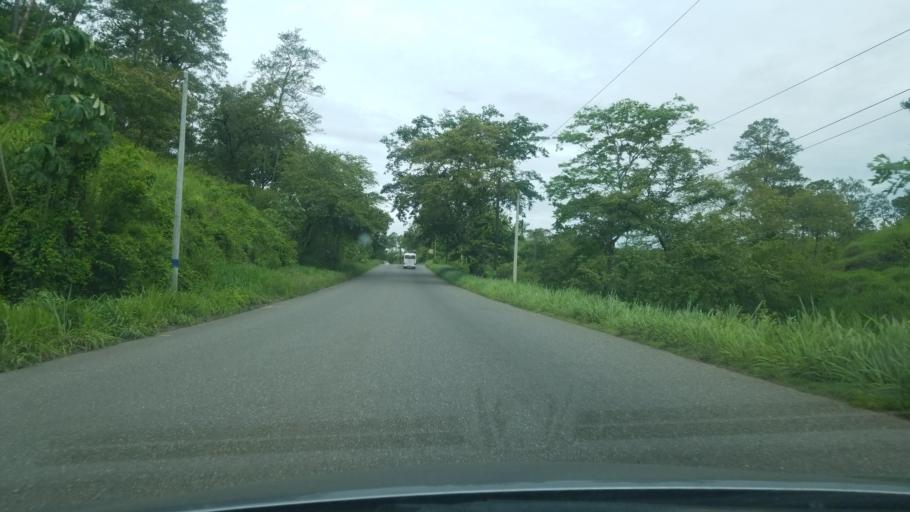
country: HN
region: Santa Barbara
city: San Marcos
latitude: 15.3046
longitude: -88.4511
